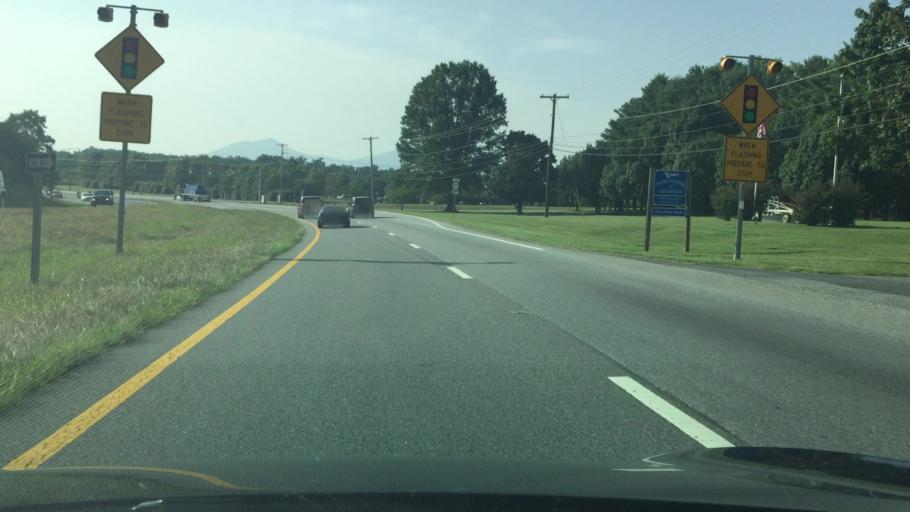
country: US
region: Virginia
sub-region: City of Bedford
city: Bedford
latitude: 37.3185
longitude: -79.4828
